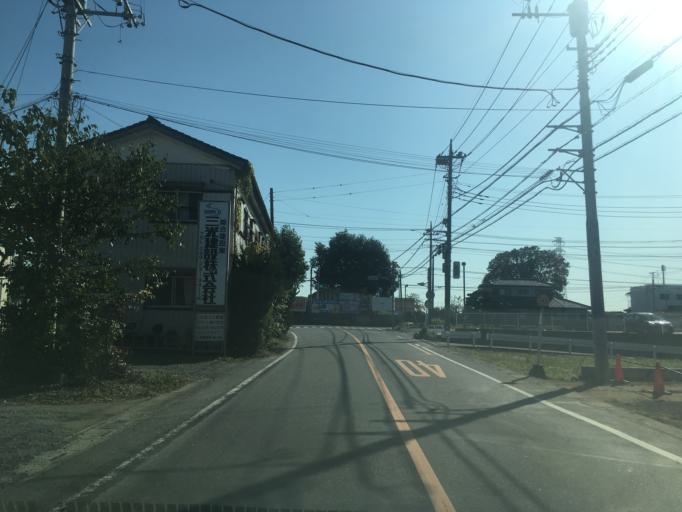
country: JP
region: Saitama
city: Kawagoe
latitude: 35.9492
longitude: 139.4504
